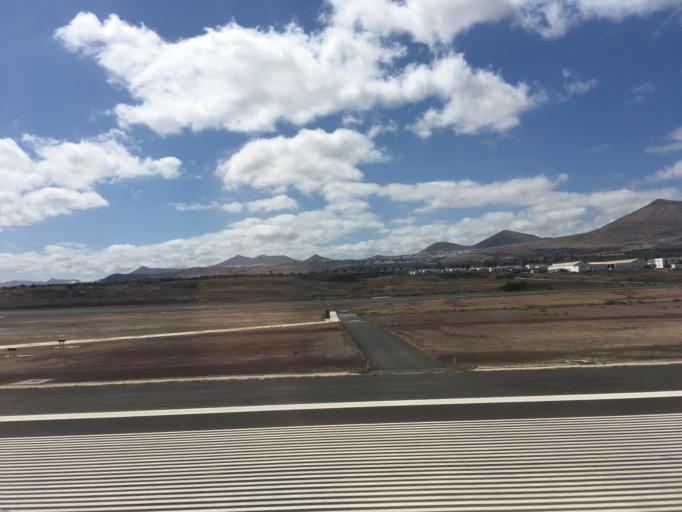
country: ES
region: Canary Islands
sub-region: Provincia de Las Palmas
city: Tias
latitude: 28.9399
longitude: -13.6085
